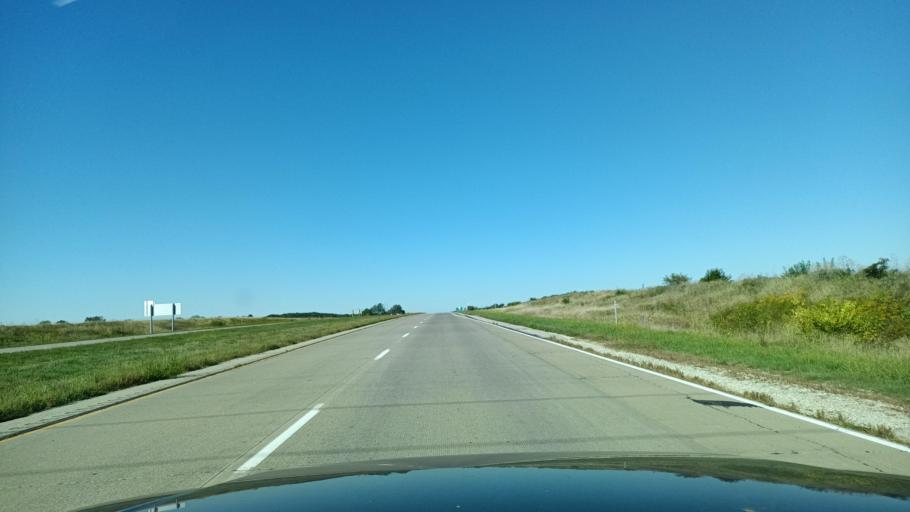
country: US
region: Iowa
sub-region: Lee County
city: Fort Madison
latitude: 40.6706
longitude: -91.3341
